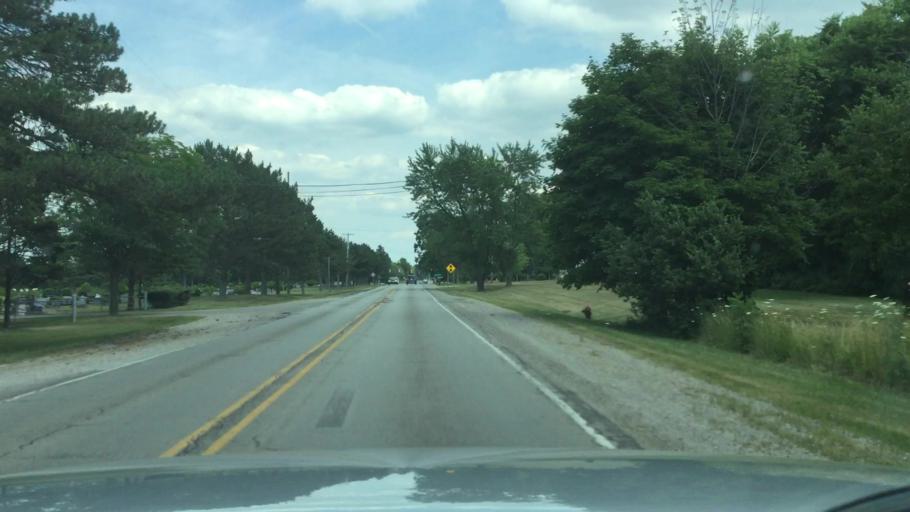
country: US
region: Michigan
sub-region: Genesee County
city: Grand Blanc
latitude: 42.9449
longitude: -83.6372
